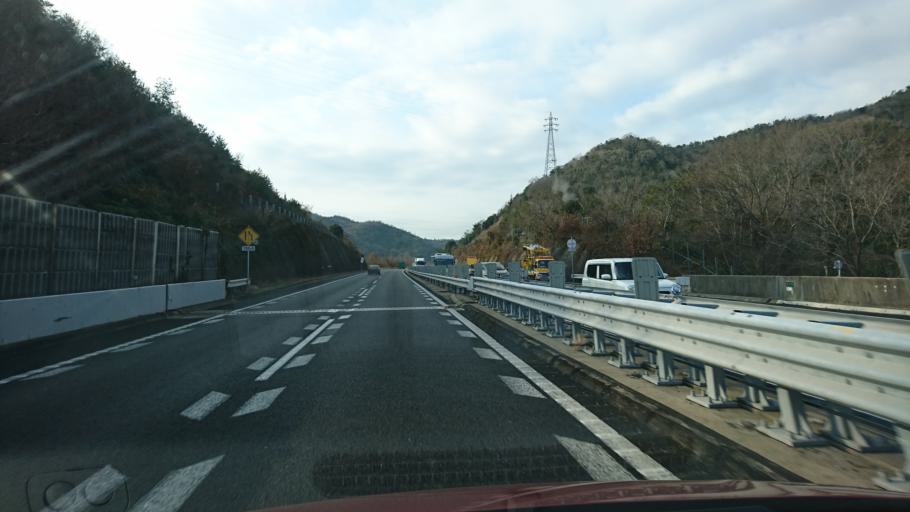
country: JP
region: Hyogo
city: Aioi
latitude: 34.8002
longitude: 134.4360
